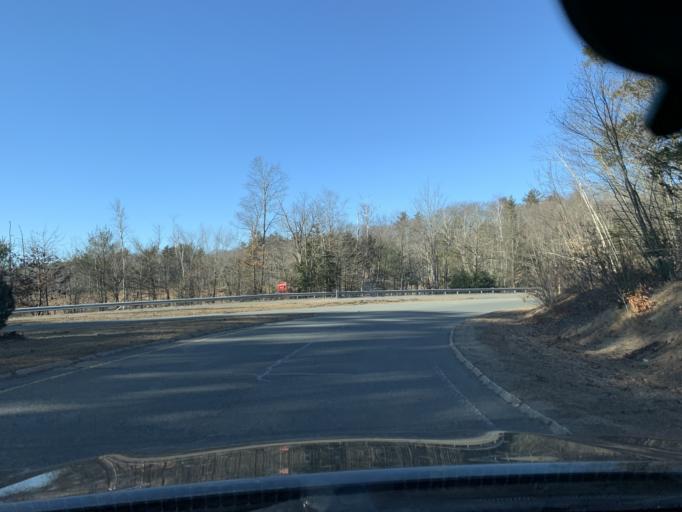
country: US
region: Massachusetts
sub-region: Essex County
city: Essex
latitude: 42.5908
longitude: -70.7945
